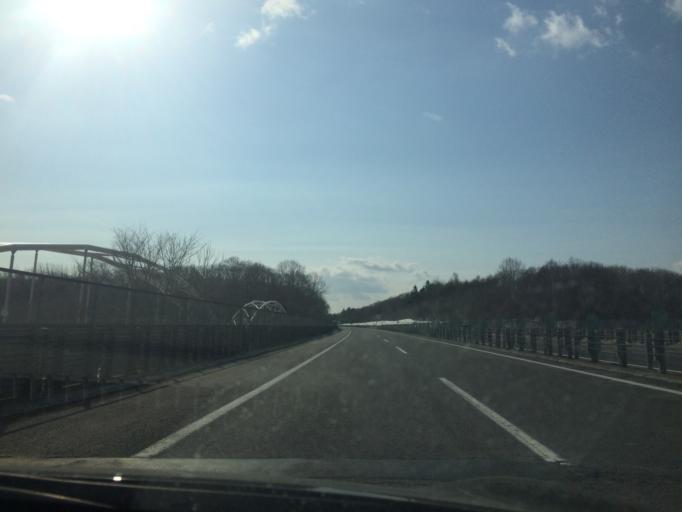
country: JP
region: Hokkaido
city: Chitose
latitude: 42.8629
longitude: 141.5583
